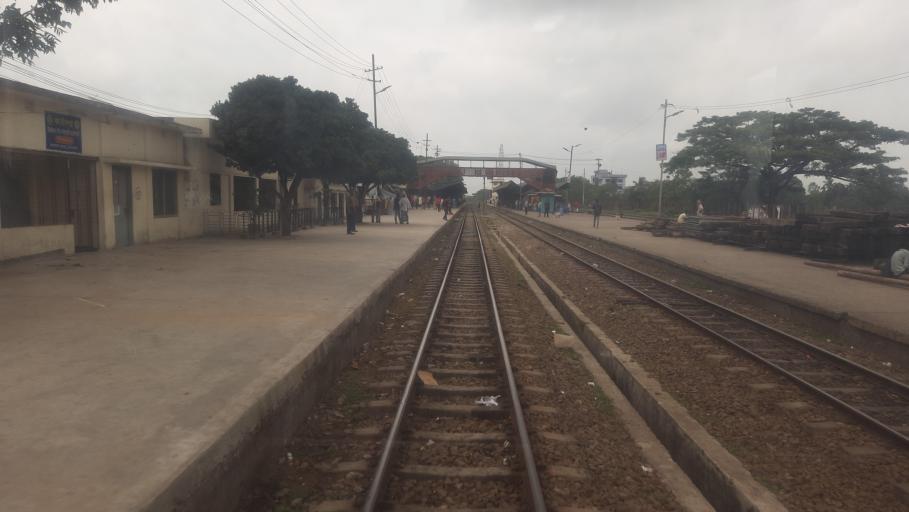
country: BD
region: Dhaka
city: Bhairab Bazar
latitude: 24.0503
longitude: 90.9793
